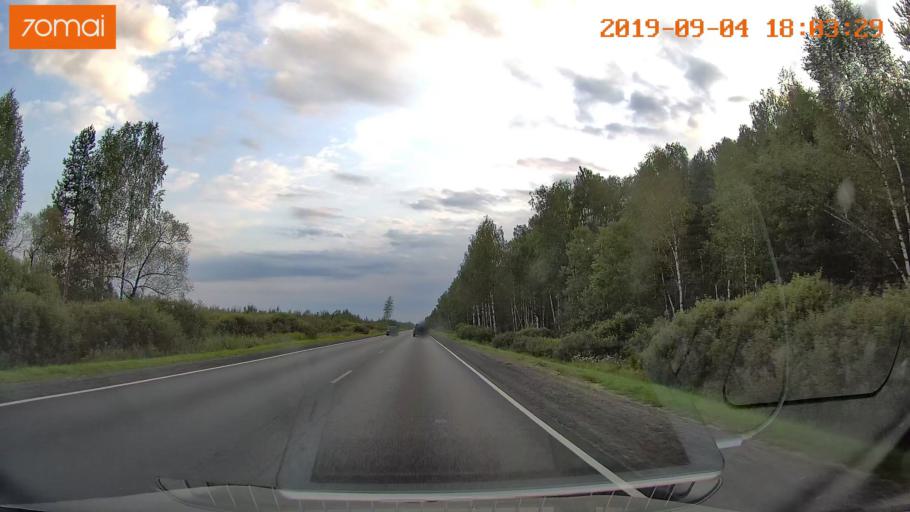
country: RU
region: Moskovskaya
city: Il'inskiy Pogost
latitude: 55.4628
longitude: 38.8514
